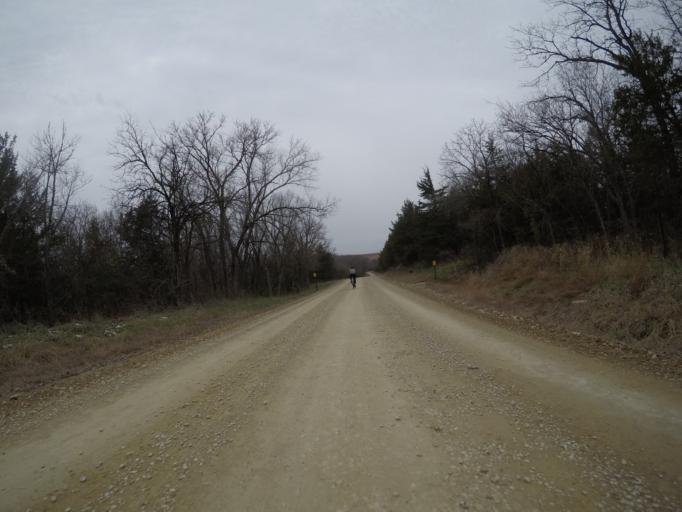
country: US
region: Kansas
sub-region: Riley County
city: Ogden
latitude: 39.1823
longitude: -96.6826
